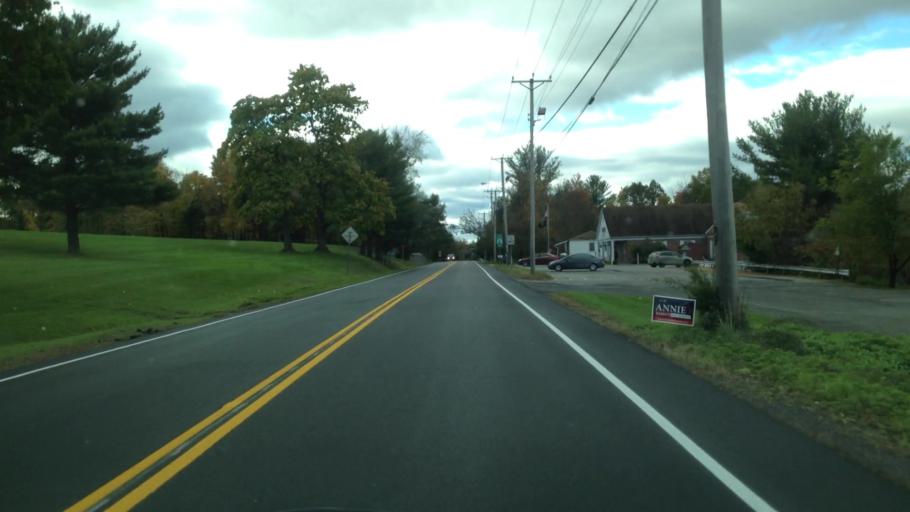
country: US
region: New York
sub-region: Ulster County
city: New Paltz
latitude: 41.7401
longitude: -74.0902
